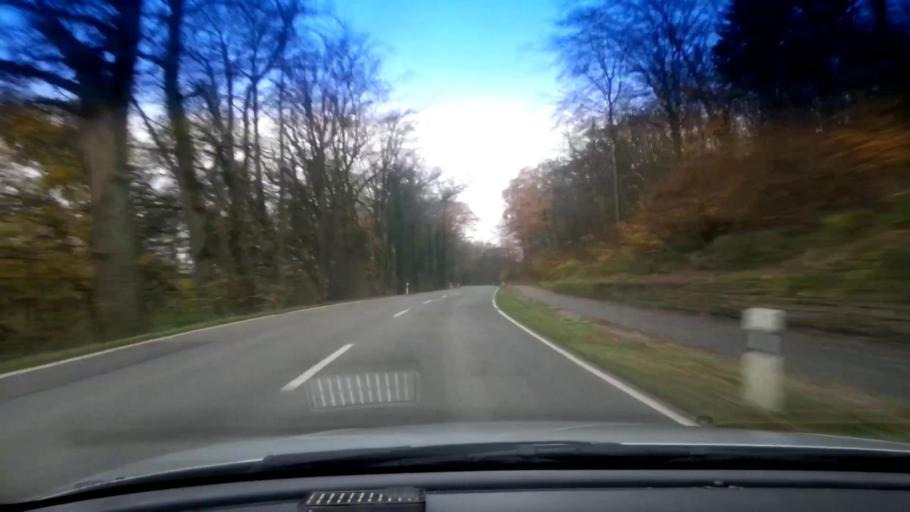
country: DE
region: Bavaria
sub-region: Upper Franconia
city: Pettstadt
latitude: 49.8551
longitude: 10.9235
